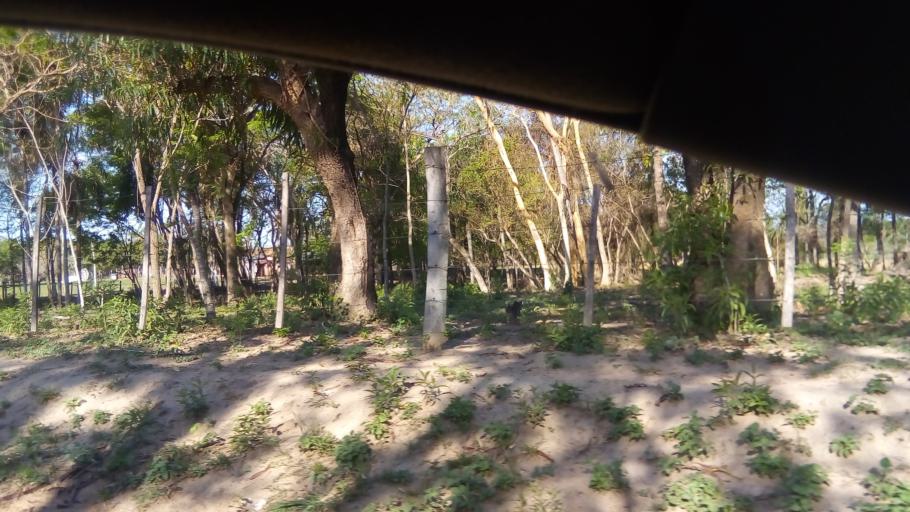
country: PY
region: Cordillera
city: Arroyos y Esteros
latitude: -24.9824
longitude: -57.1992
